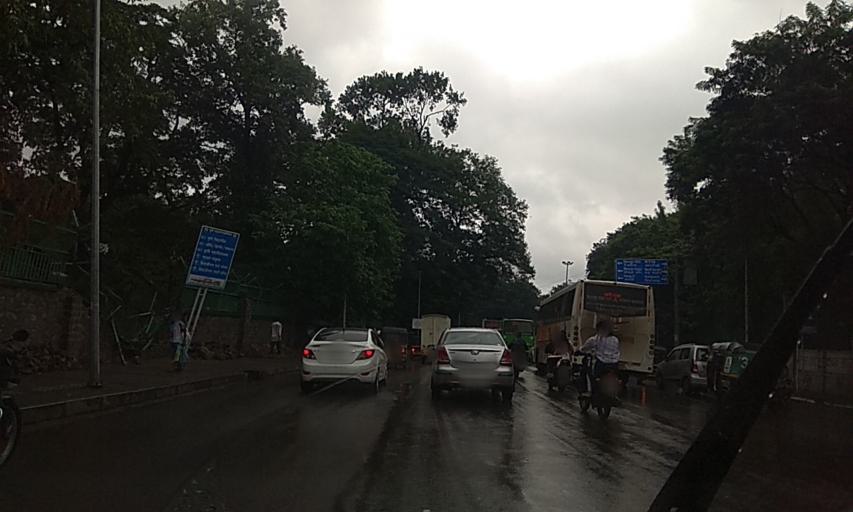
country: IN
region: Maharashtra
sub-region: Pune Division
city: Shivaji Nagar
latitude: 18.5291
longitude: 73.8499
